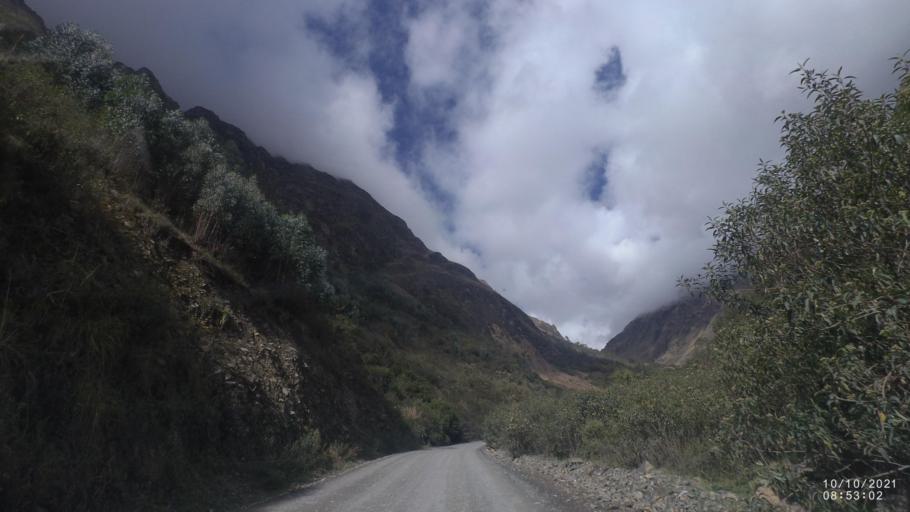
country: BO
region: La Paz
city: Quime
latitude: -16.9873
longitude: -67.2310
